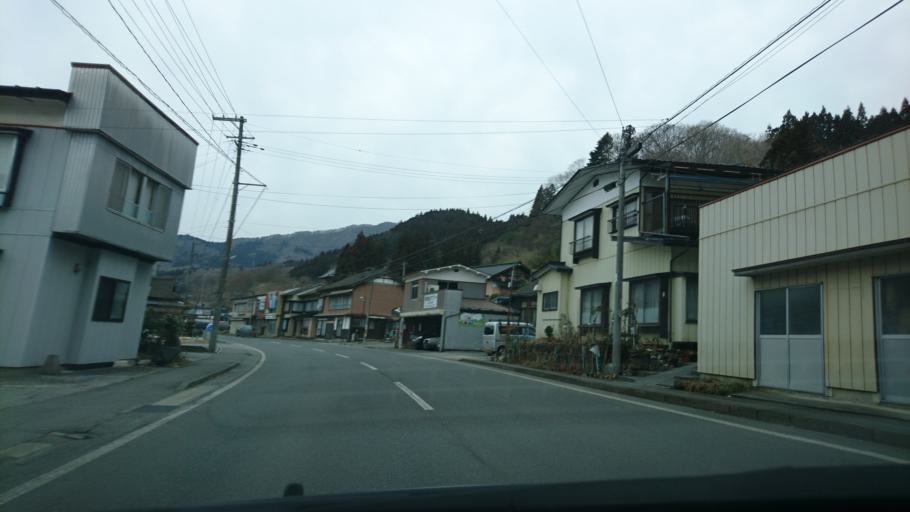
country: JP
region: Iwate
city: Ofunato
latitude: 39.1453
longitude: 141.5785
